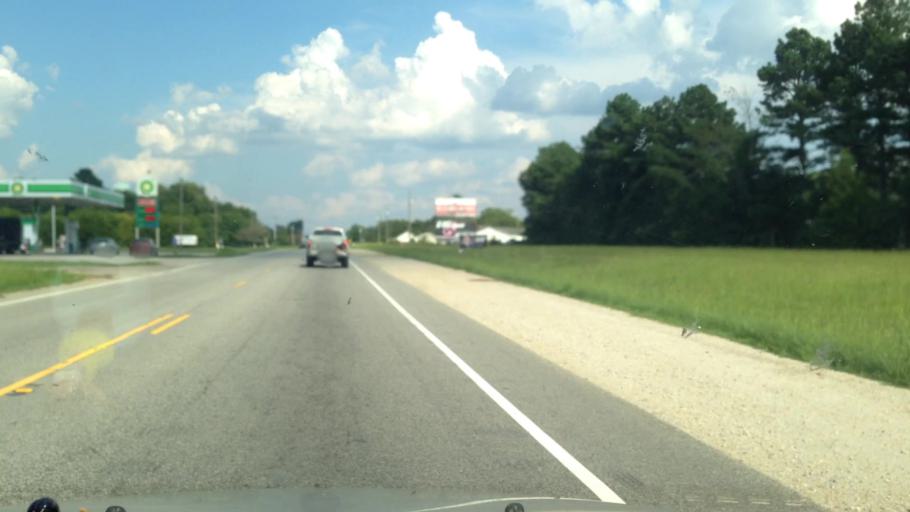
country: US
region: North Carolina
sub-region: Lee County
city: Broadway
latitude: 35.4378
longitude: -79.0319
